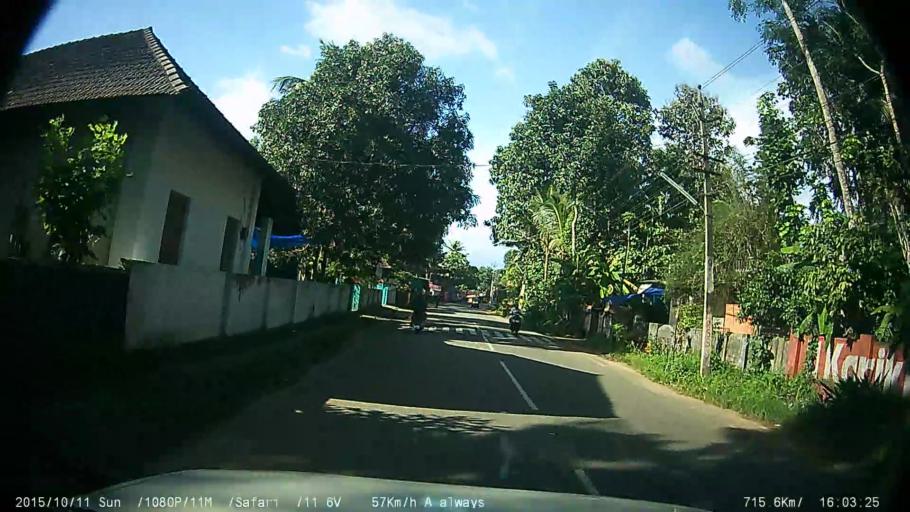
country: IN
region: Kerala
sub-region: Kottayam
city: Palackattumala
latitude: 9.6702
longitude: 76.6107
